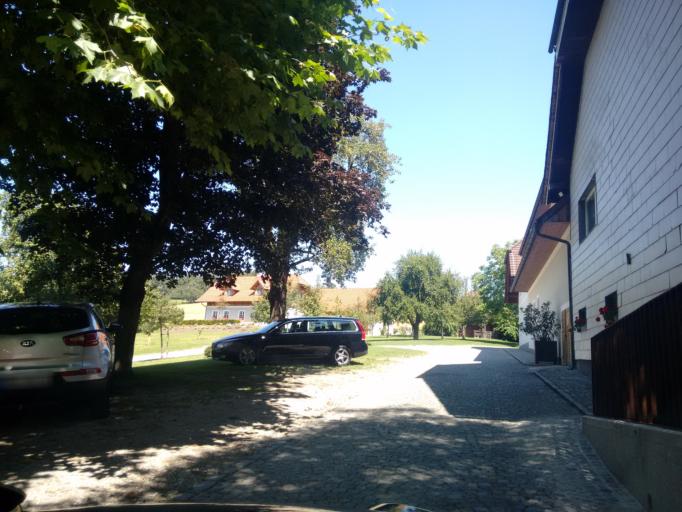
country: AT
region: Upper Austria
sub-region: Wels-Land
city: Gunskirchen
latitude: 48.1755
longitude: 13.9466
